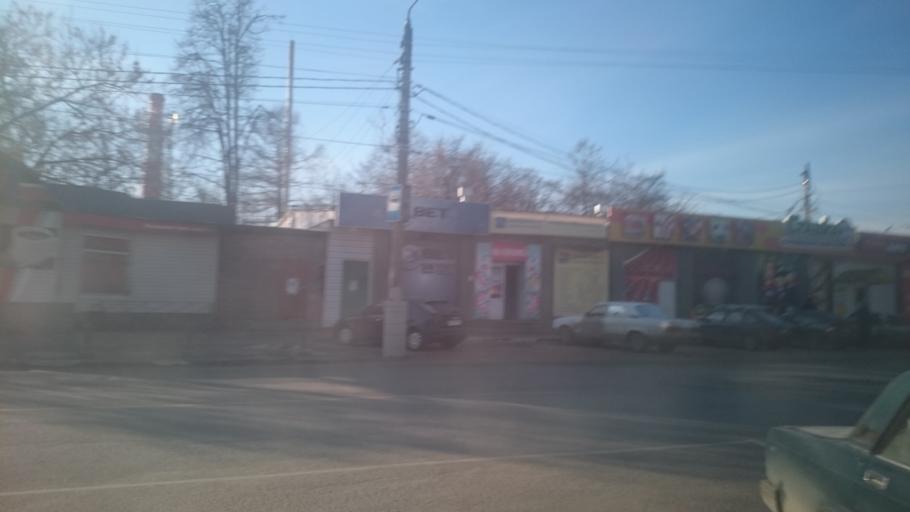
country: RU
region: Tula
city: Tula
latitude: 54.1764
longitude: 37.6307
